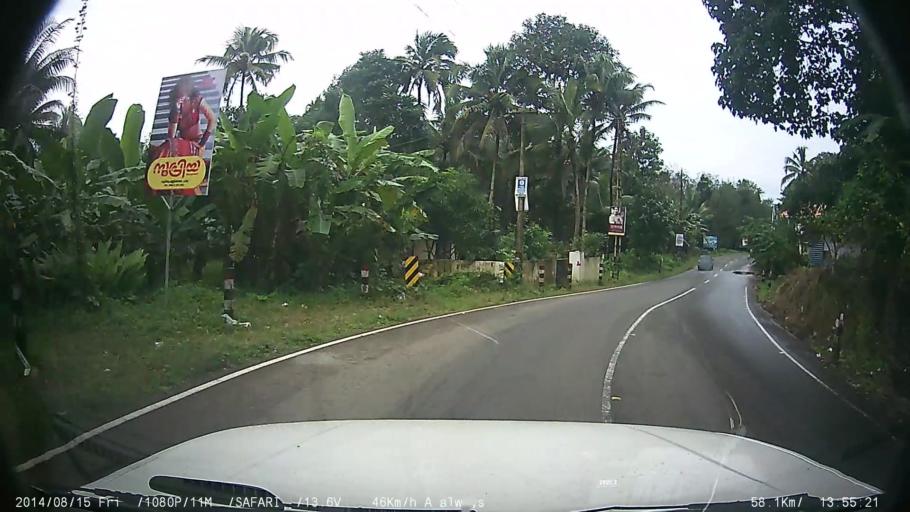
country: IN
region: Kerala
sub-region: Kottayam
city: Palackattumala
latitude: 9.7196
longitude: 76.6556
